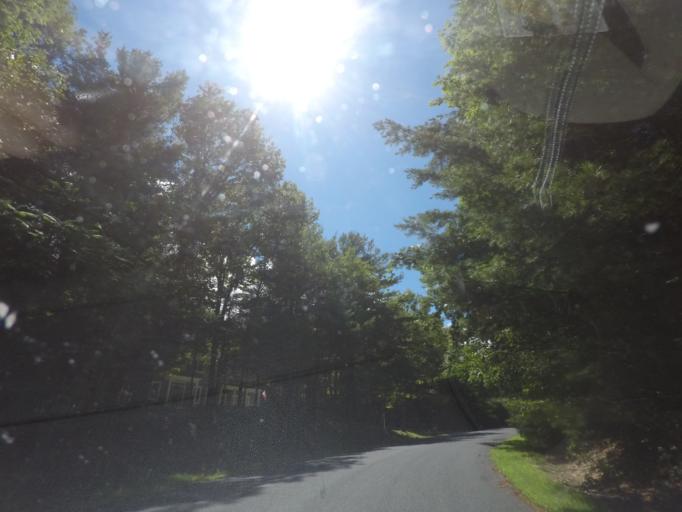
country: US
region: New York
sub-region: Rensselaer County
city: Averill Park
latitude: 42.6269
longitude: -73.5782
